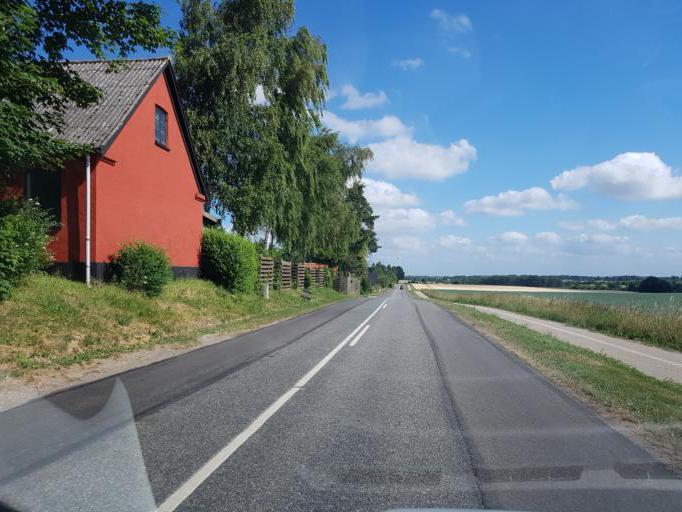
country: DK
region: Zealand
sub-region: Lejre Kommune
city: Osted
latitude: 55.5792
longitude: 11.9675
